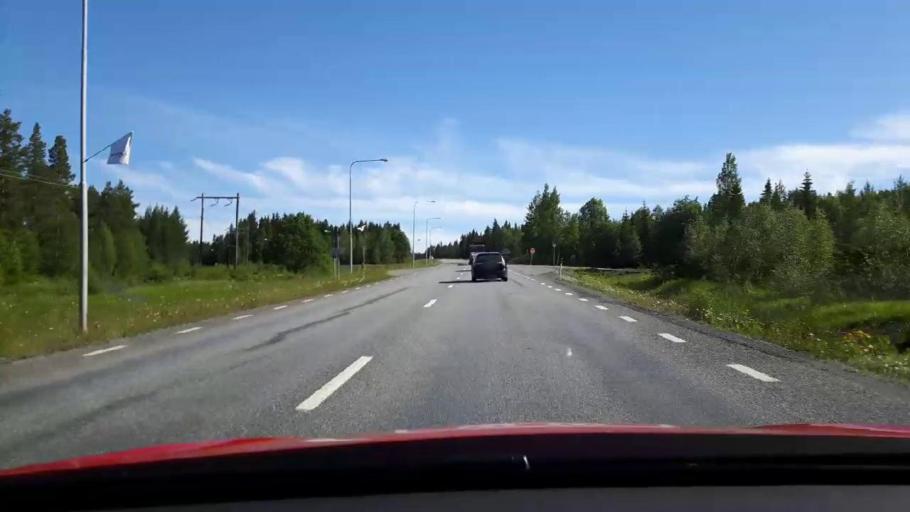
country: SE
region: Jaemtland
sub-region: OEstersunds Kommun
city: Lit
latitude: 63.3789
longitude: 14.8865
